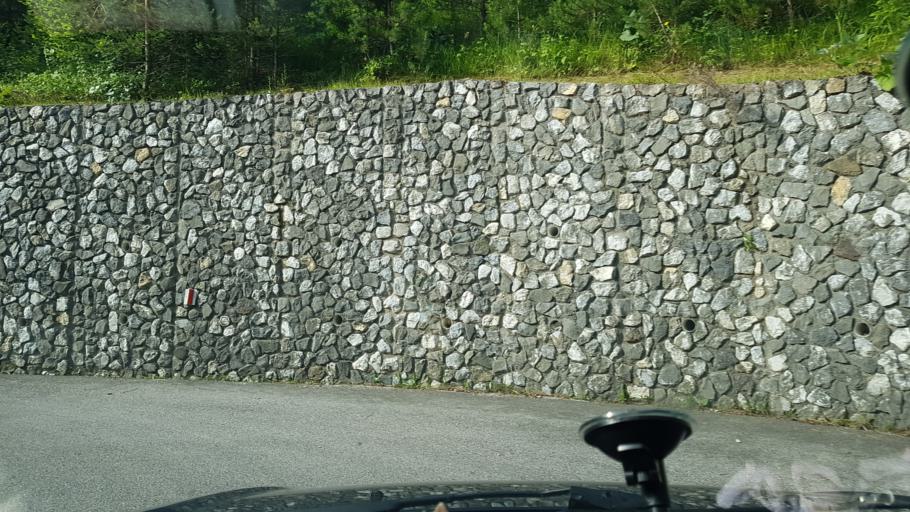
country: IT
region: Friuli Venezia Giulia
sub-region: Provincia di Udine
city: Prato
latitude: 46.3634
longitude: 13.3387
